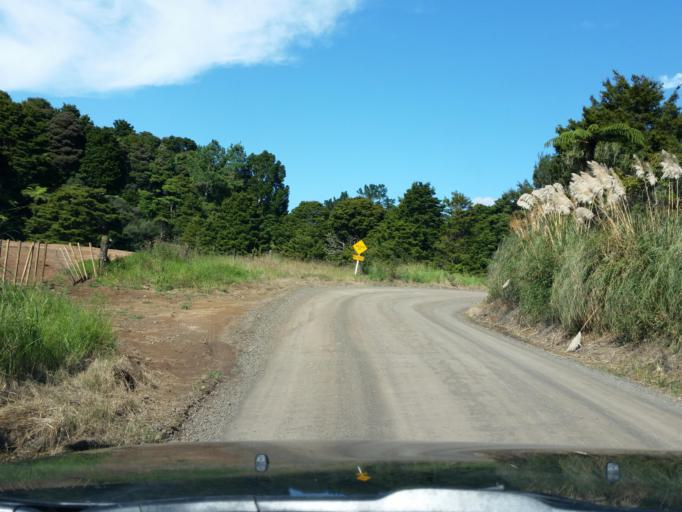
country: NZ
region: Northland
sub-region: Kaipara District
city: Dargaville
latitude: -35.7098
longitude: 173.6230
